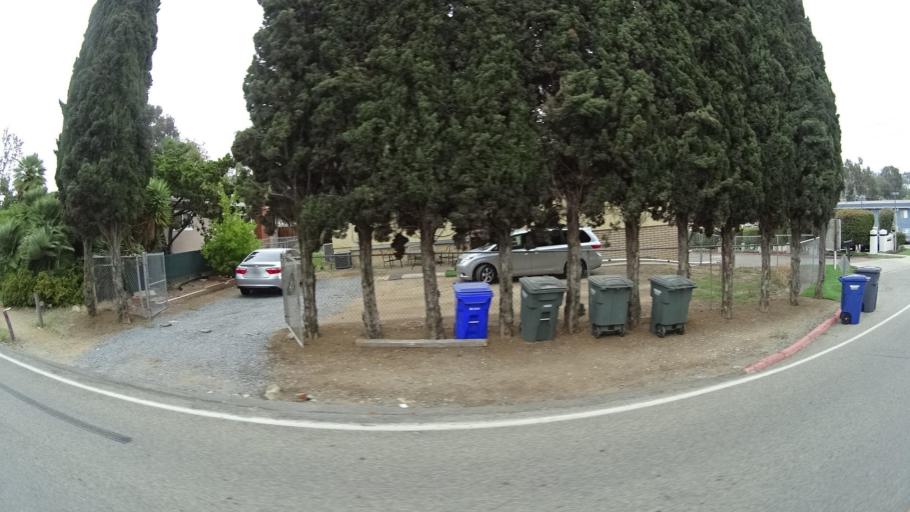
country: US
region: California
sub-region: San Diego County
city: Spring Valley
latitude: 32.7510
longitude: -116.9874
